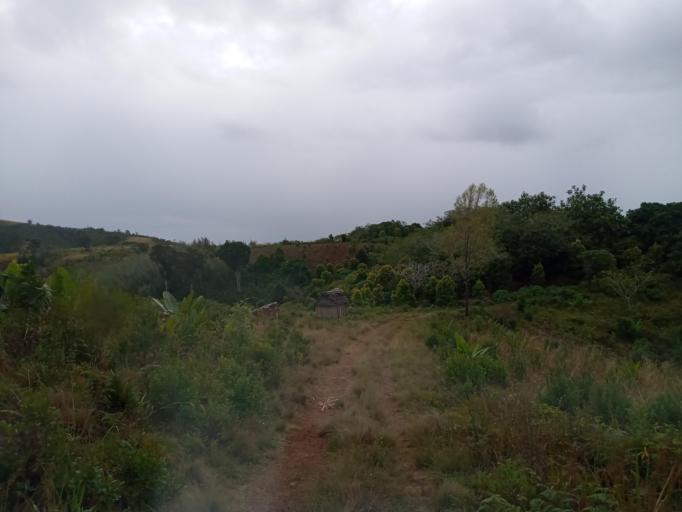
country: MG
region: Atsimo-Atsinanana
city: Vohipaho
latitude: -23.9948
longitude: 47.4015
